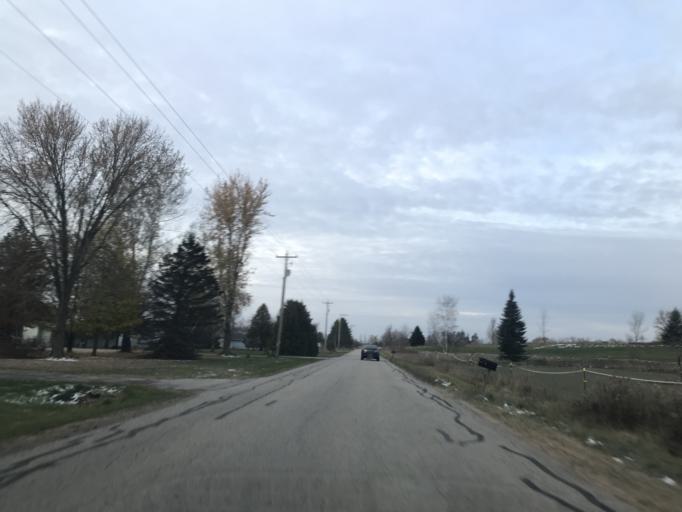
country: US
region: Wisconsin
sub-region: Marinette County
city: Peshtigo
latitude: 45.0573
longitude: -87.7950
